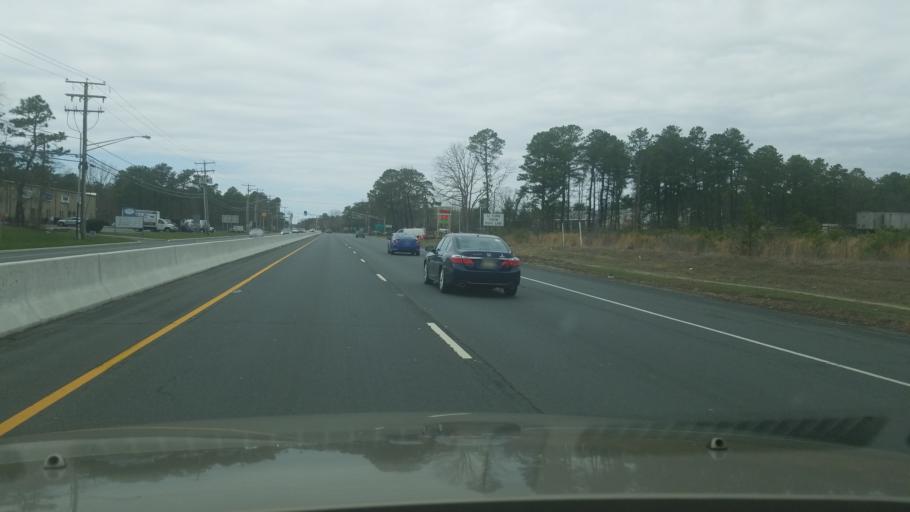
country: US
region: New Jersey
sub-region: Ocean County
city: Leisure Village West-Pine Lake Park
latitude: 39.9889
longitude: -74.2647
